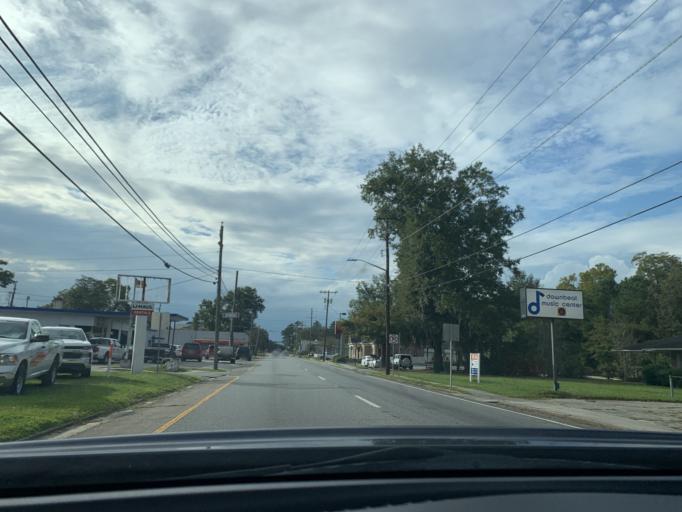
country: US
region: Georgia
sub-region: Chatham County
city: Pooler
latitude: 32.1152
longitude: -81.2460
